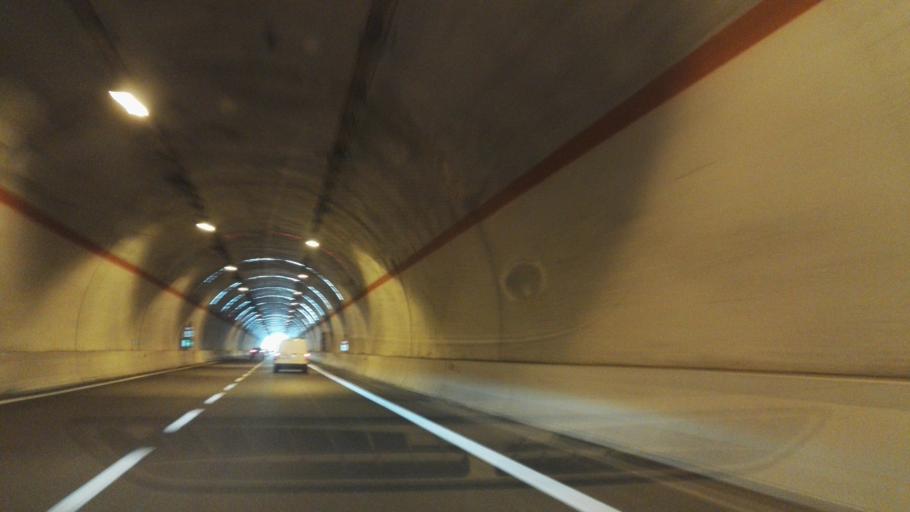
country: IT
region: Calabria
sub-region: Provincia di Catanzaro
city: Squillace Lido
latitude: 38.8068
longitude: 16.5571
